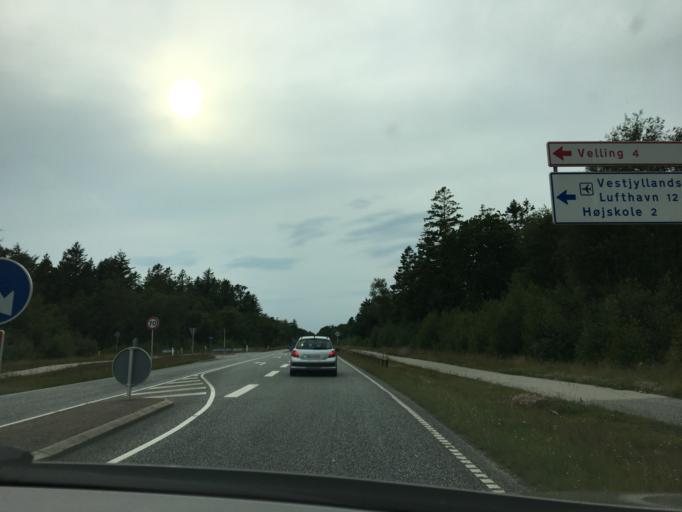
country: DK
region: Central Jutland
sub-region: Ringkobing-Skjern Kommune
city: Ringkobing
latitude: 56.0835
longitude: 8.3308
